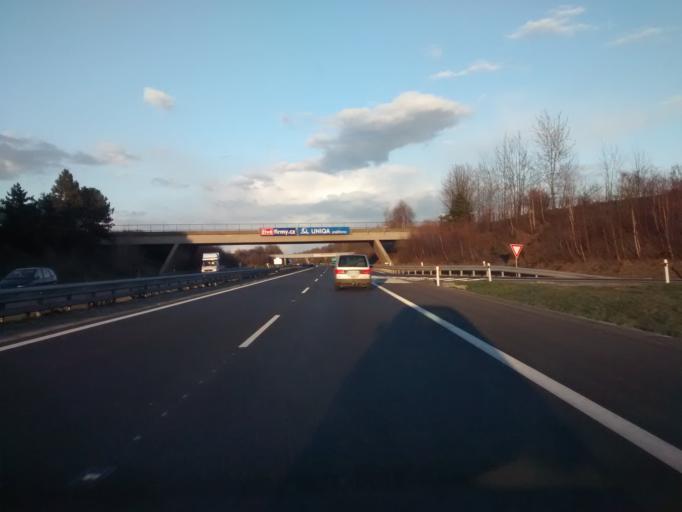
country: CZ
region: Central Bohemia
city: Jirny
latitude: 50.1224
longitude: 14.7026
